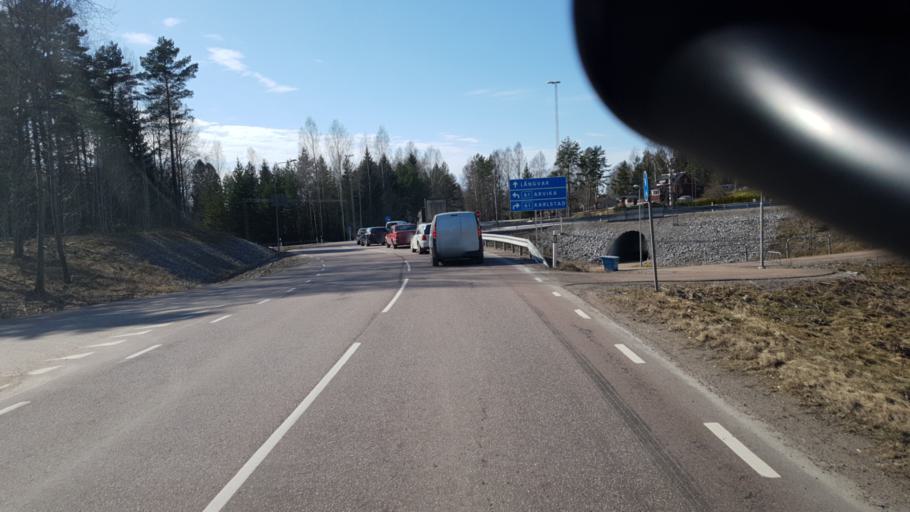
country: SE
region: Vaermland
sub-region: Arvika Kommun
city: Arvika
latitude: 59.6475
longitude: 12.7501
